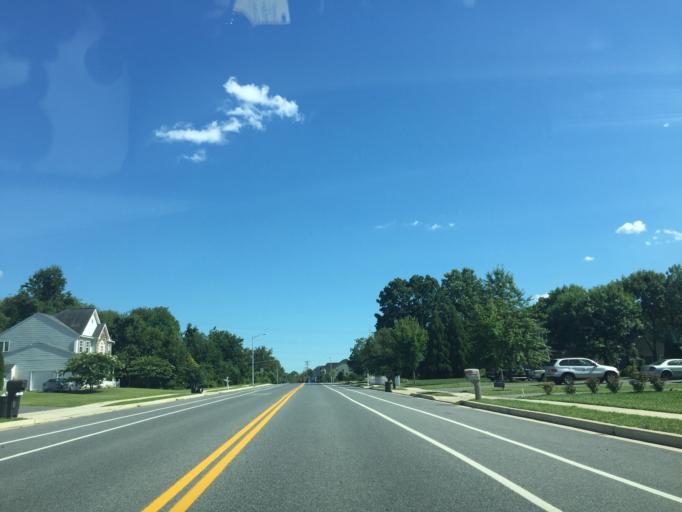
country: US
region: Maryland
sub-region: Baltimore County
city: White Marsh
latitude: 39.4052
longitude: -76.4104
